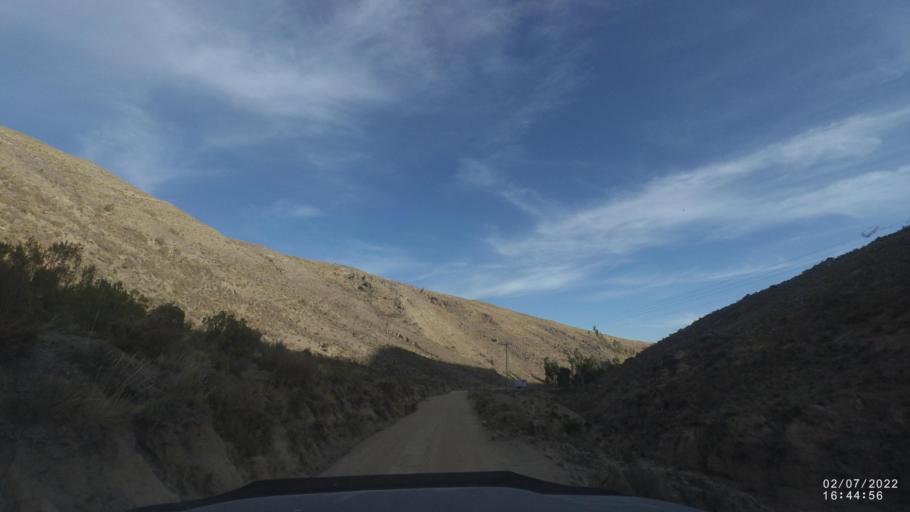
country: BO
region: Cochabamba
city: Irpa Irpa
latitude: -17.9737
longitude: -66.5097
